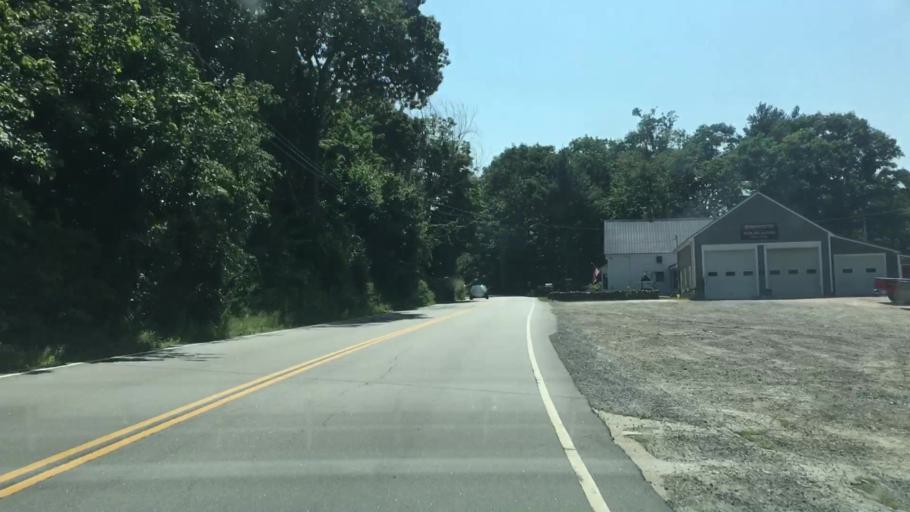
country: US
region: New Hampshire
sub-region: Rockingham County
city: Hampstead
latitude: 42.8635
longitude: -71.2240
